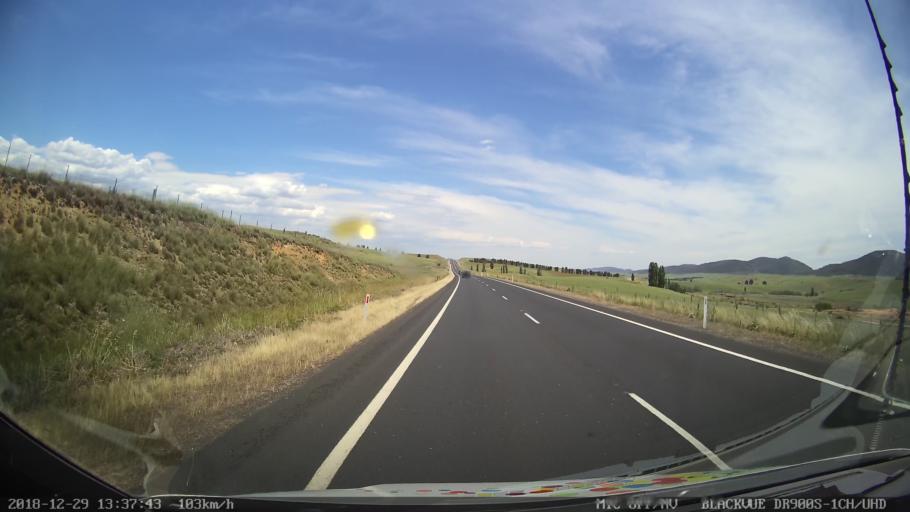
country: AU
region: New South Wales
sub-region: Cooma-Monaro
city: Cooma
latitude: -35.9881
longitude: 149.1378
